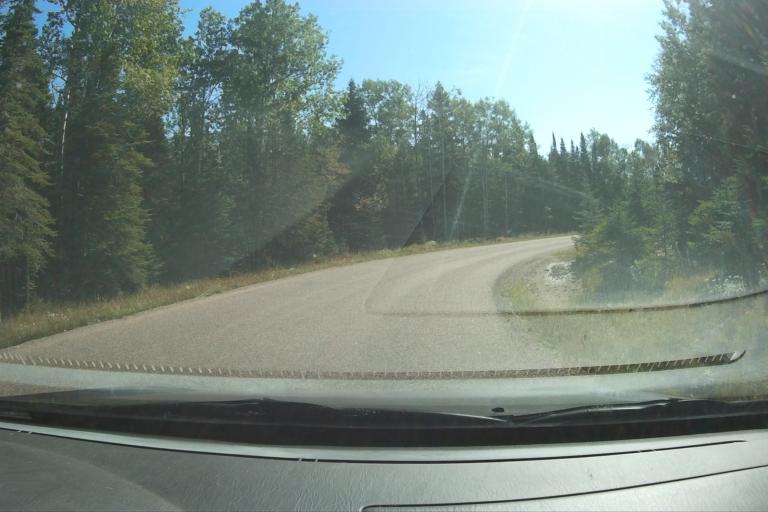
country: CA
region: Ontario
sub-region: Thunder Bay District
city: Thunder Bay
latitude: 48.3468
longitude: -88.7973
